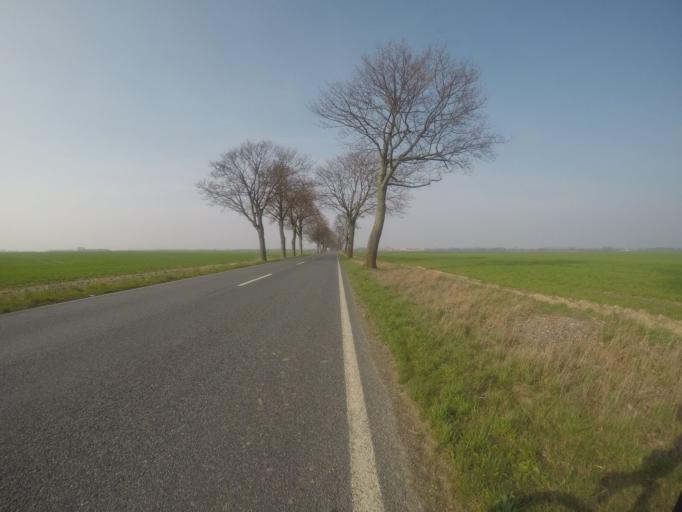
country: DE
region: Brandenburg
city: Schonefeld
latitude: 52.3219
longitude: 13.5068
